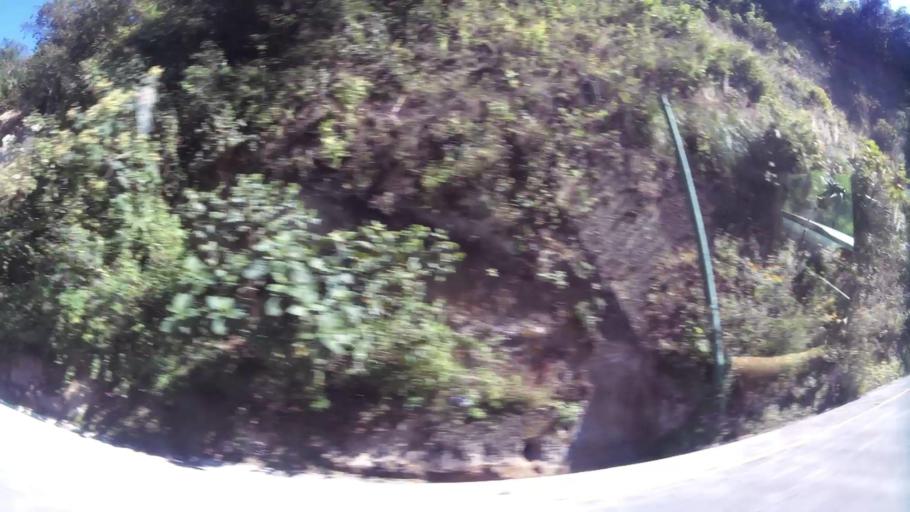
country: GT
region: Sacatepequez
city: Santa Lucia Milpas Altas
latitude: 14.5735
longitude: -90.6880
